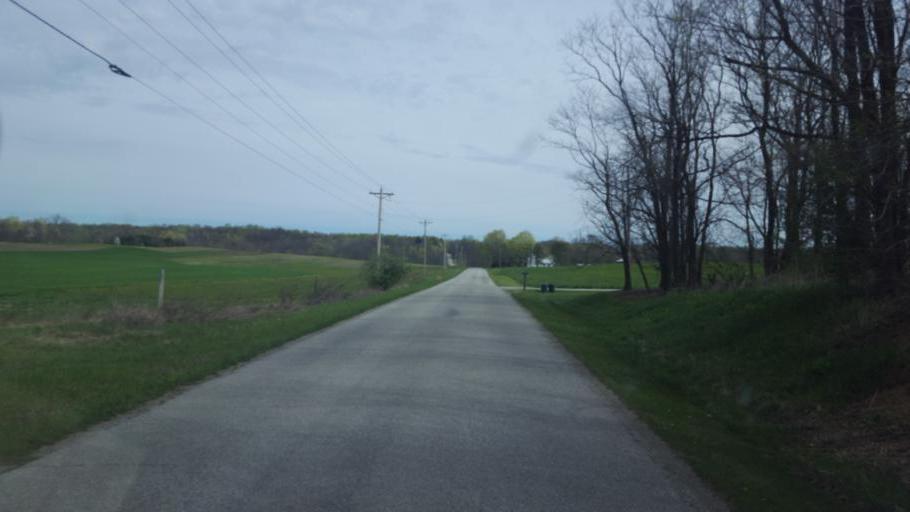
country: US
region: Ohio
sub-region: Knox County
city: Fredericktown
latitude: 40.4732
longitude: -82.6468
